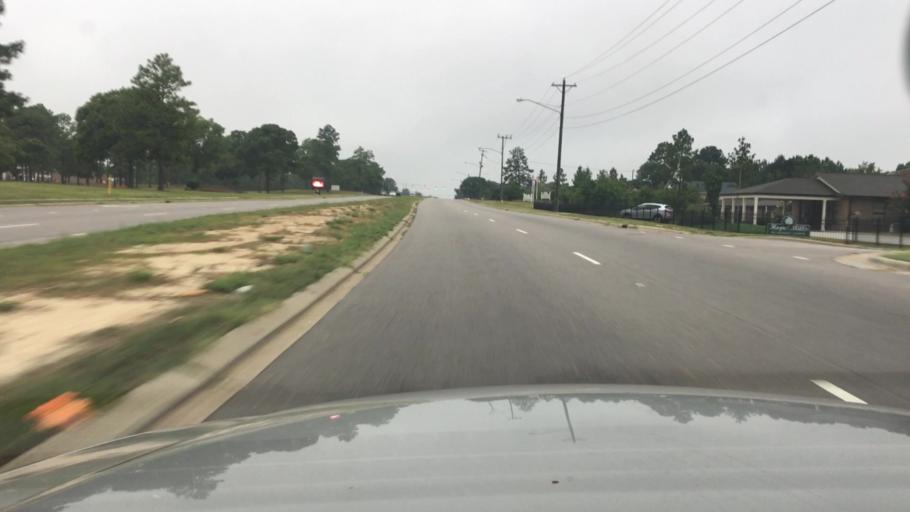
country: US
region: North Carolina
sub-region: Cumberland County
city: Hope Mills
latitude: 34.9790
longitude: -78.9249
